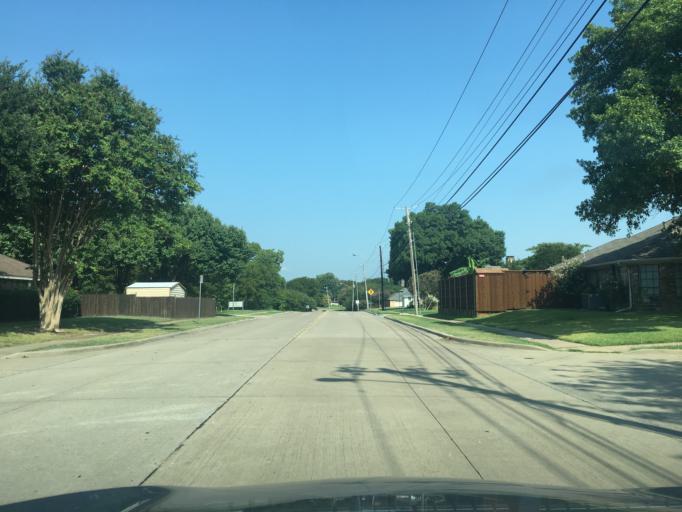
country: US
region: Texas
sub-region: Dallas County
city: Garland
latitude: 32.9440
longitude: -96.6355
